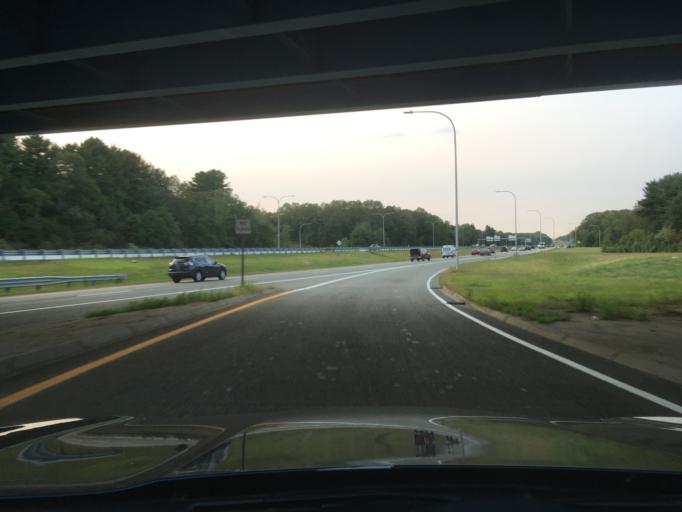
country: US
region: Rhode Island
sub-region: Kent County
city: East Greenwich
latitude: 41.6292
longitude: -71.4865
